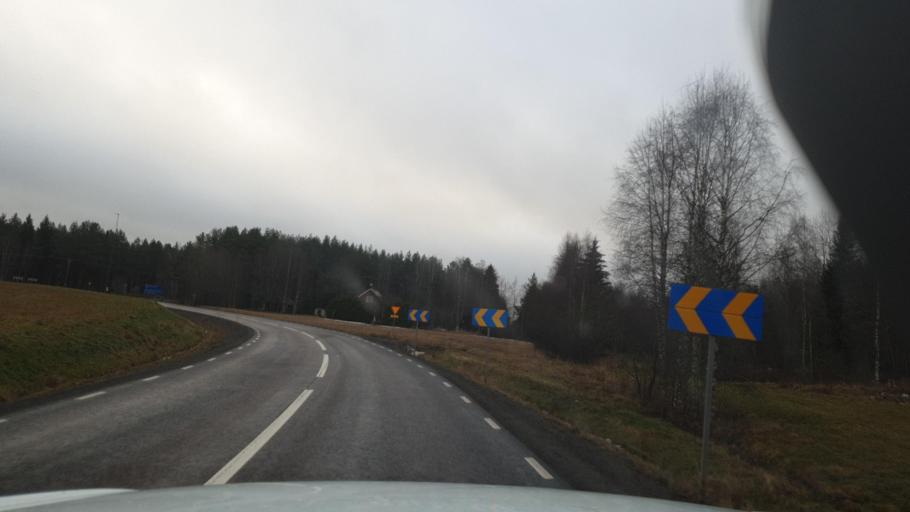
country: SE
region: Vaermland
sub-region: Arjangs Kommun
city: Arjaeng
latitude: 59.5548
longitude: 12.1186
